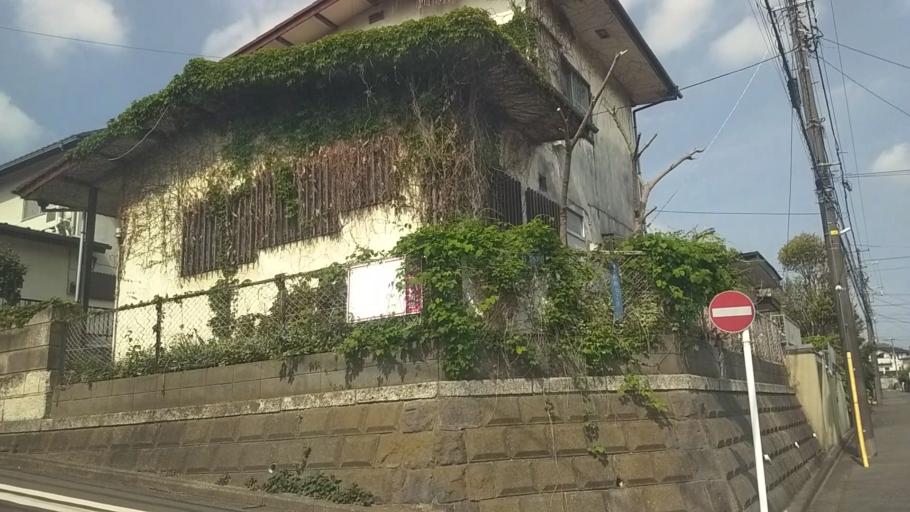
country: JP
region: Kanagawa
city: Yokohama
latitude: 35.3736
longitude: 139.6166
